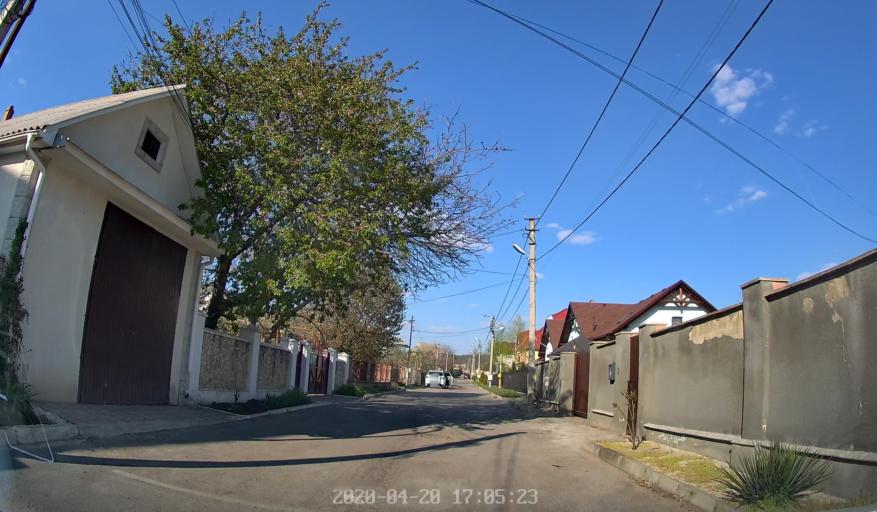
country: MD
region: Chisinau
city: Chisinau
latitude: 46.9593
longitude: 28.8382
